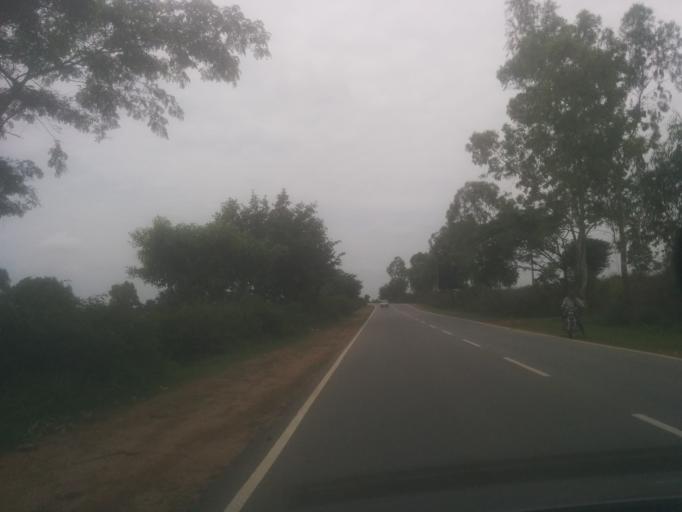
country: IN
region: Karnataka
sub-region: Hassan
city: Belur
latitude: 13.1628
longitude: 75.8962
